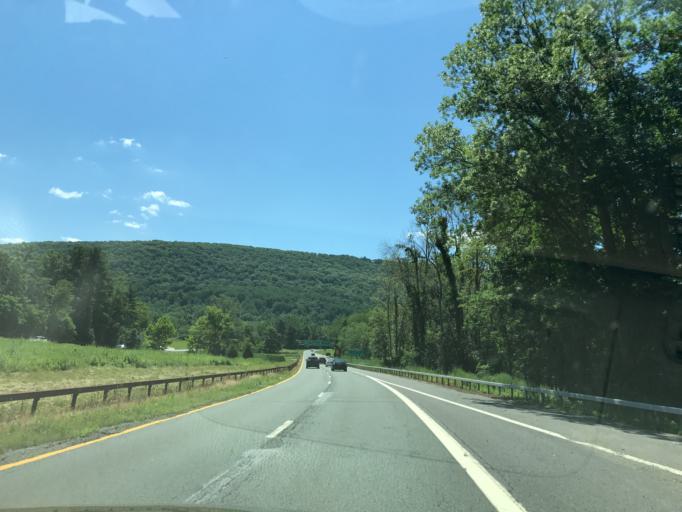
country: US
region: New York
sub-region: Dutchess County
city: Hillside Lake
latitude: 41.5445
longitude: -73.7752
